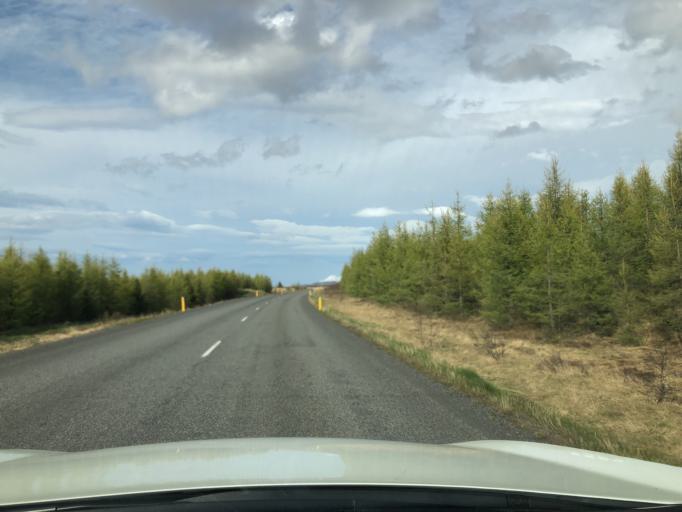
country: IS
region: East
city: Egilsstadir
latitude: 65.1830
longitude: -14.5060
